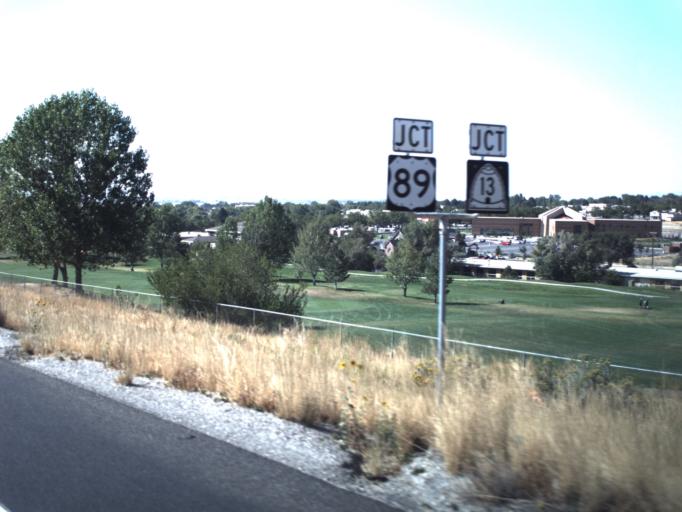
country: US
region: Utah
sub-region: Box Elder County
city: Brigham City
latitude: 41.4866
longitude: -112.0109
